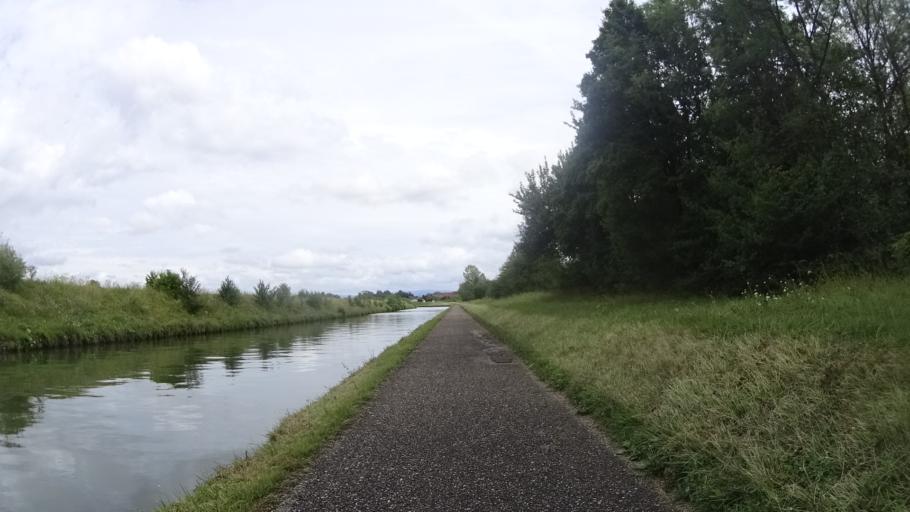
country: FR
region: Lorraine
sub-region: Departement de la Moselle
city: Lorquin
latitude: 48.6905
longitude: 6.9201
